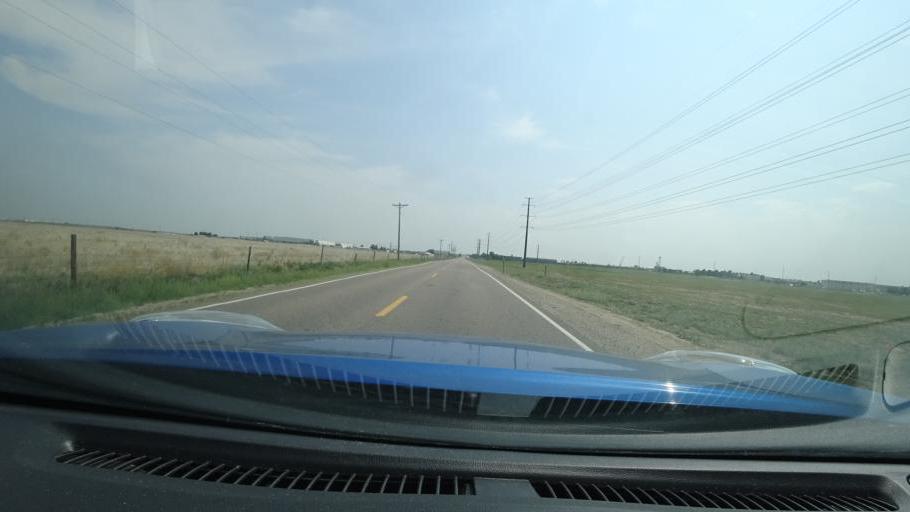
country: US
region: Colorado
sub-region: Adams County
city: Aurora
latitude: 39.7610
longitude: -104.7346
